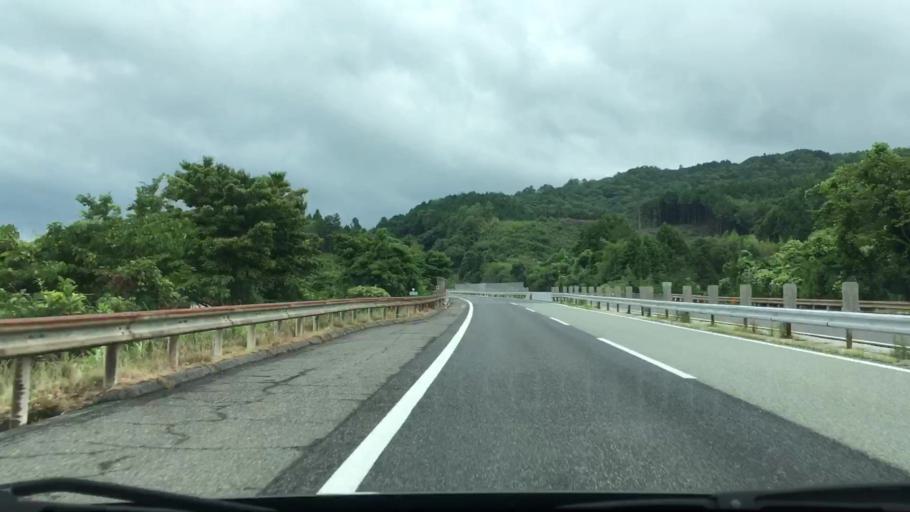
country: JP
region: Okayama
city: Niimi
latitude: 34.9422
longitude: 133.3286
